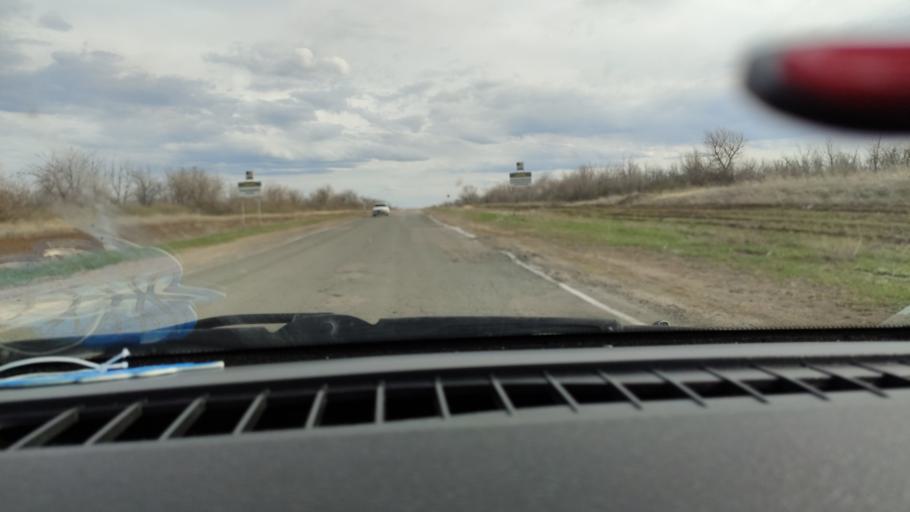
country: RU
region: Saratov
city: Rovnoye
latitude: 50.9527
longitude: 46.1223
